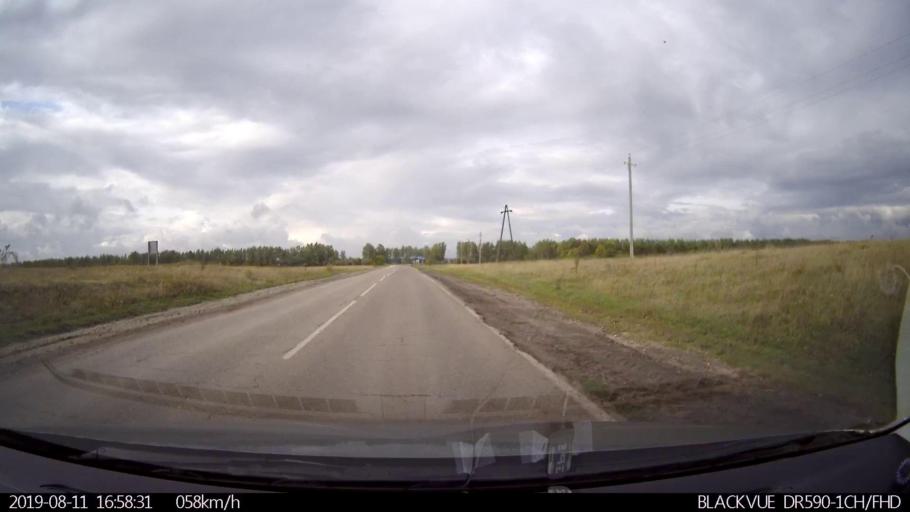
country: RU
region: Ulyanovsk
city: Mayna
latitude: 54.3073
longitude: 47.6548
